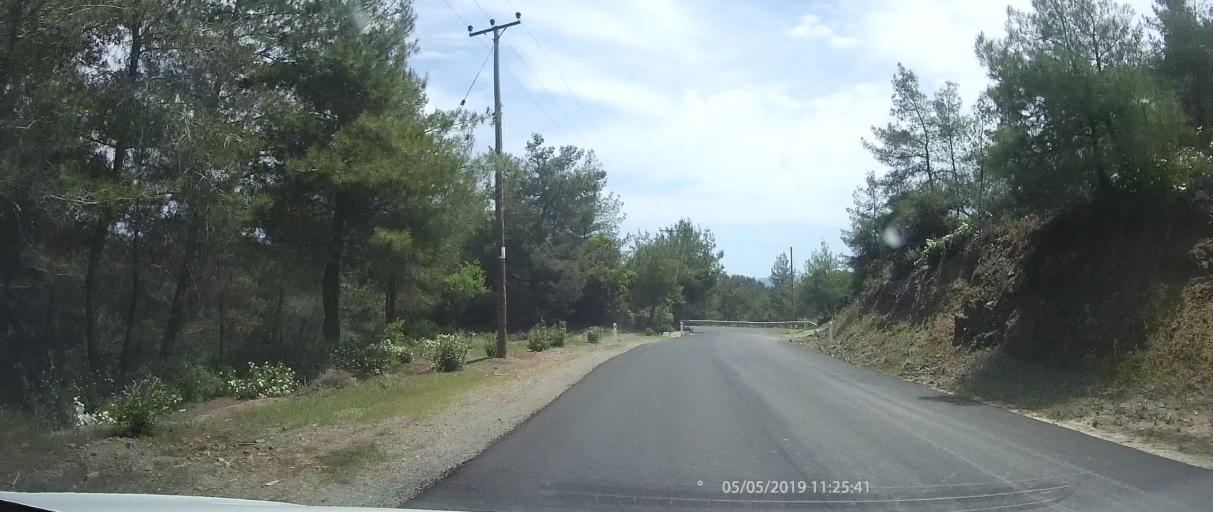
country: CY
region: Limassol
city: Pachna
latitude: 34.9240
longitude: 32.6461
